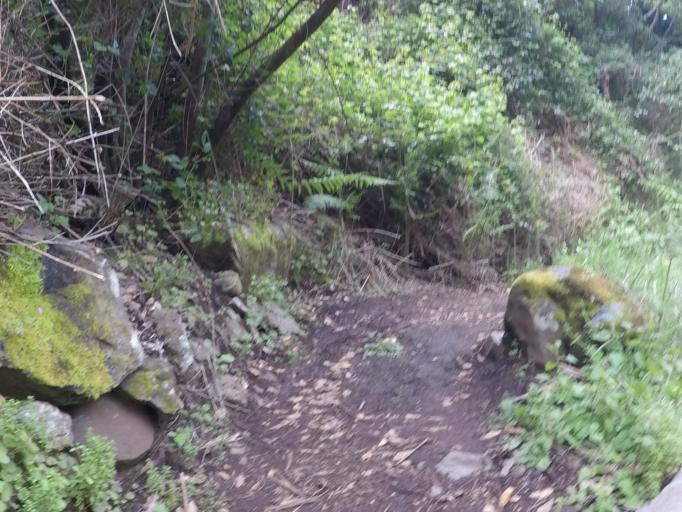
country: PT
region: Madeira
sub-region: Camara de Lobos
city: Curral das Freiras
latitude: 32.7450
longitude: -16.9983
